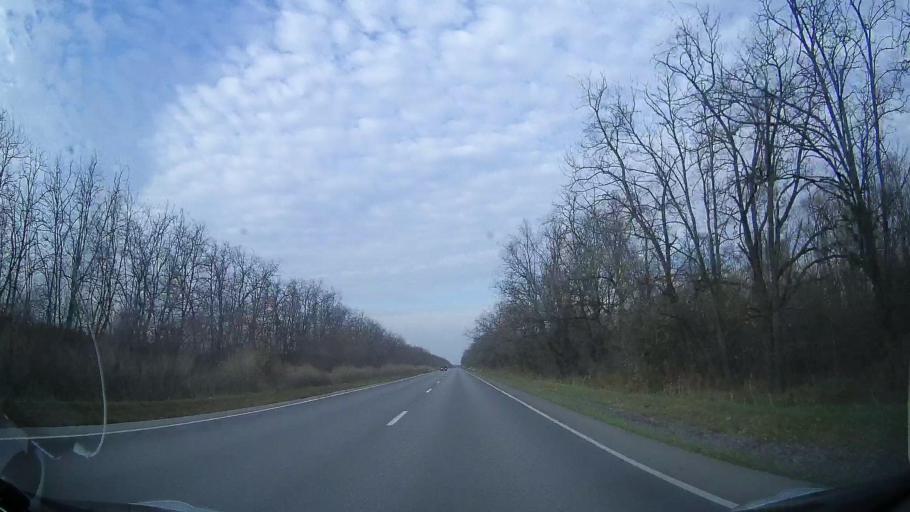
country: RU
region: Rostov
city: Bagayevskaya
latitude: 47.1162
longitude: 40.2767
